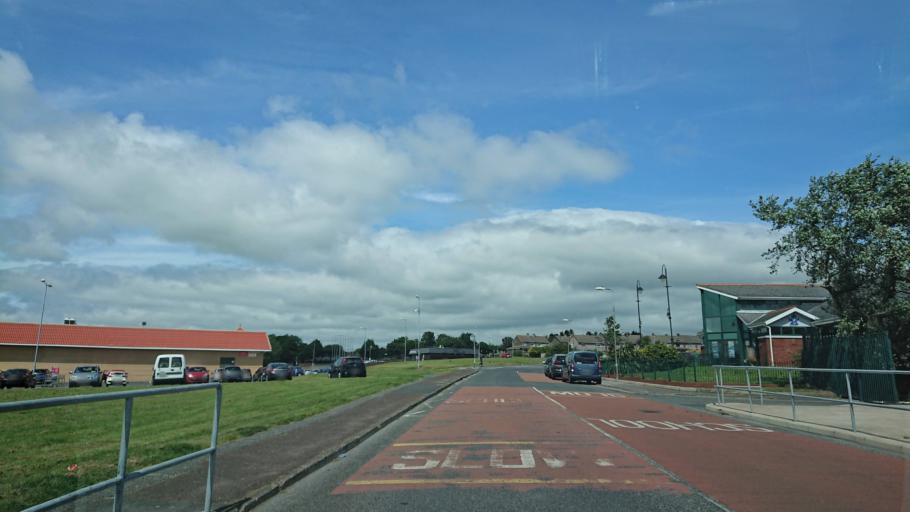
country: IE
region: Munster
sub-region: Waterford
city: Waterford
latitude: 52.2495
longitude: -7.1347
